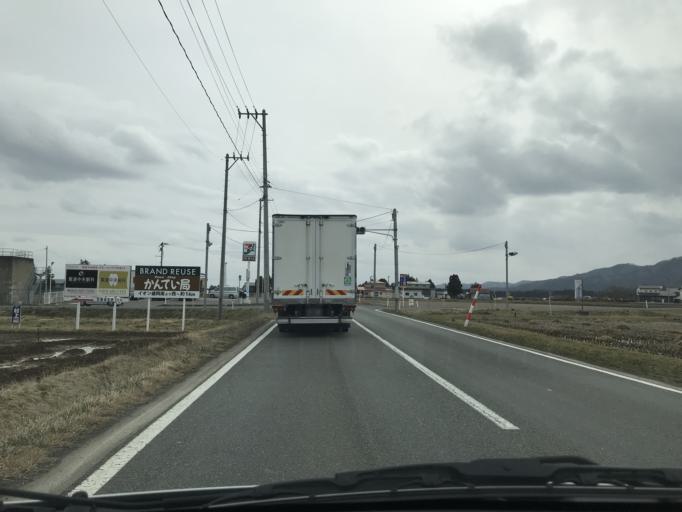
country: JP
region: Iwate
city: Morioka-shi
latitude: 39.5581
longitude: 141.1346
